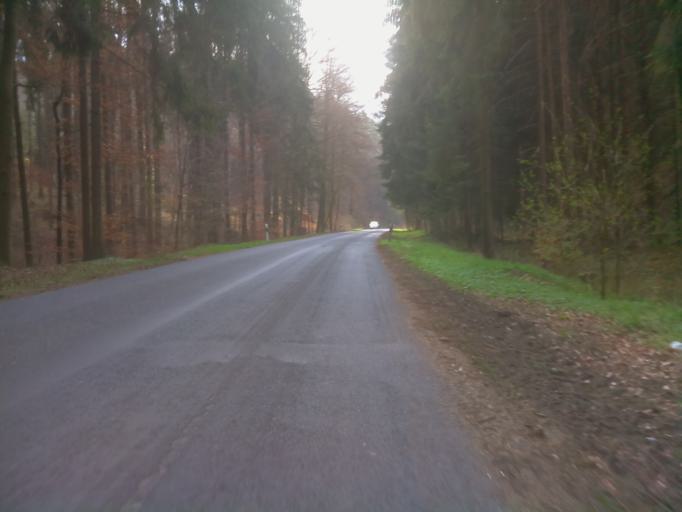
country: DE
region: Thuringia
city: Grosseutersdorf
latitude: 50.7726
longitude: 11.5634
